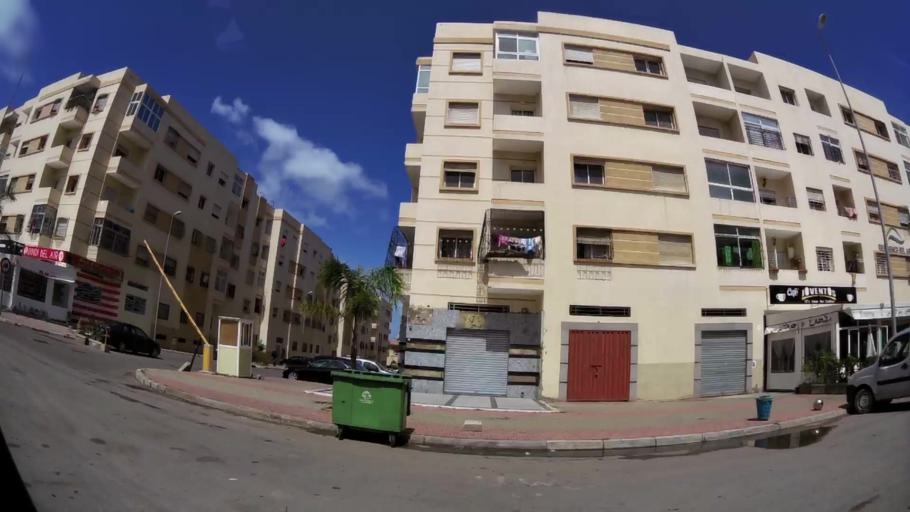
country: MA
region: Grand Casablanca
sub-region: Mediouna
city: Tit Mellil
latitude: 33.6314
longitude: -7.4557
